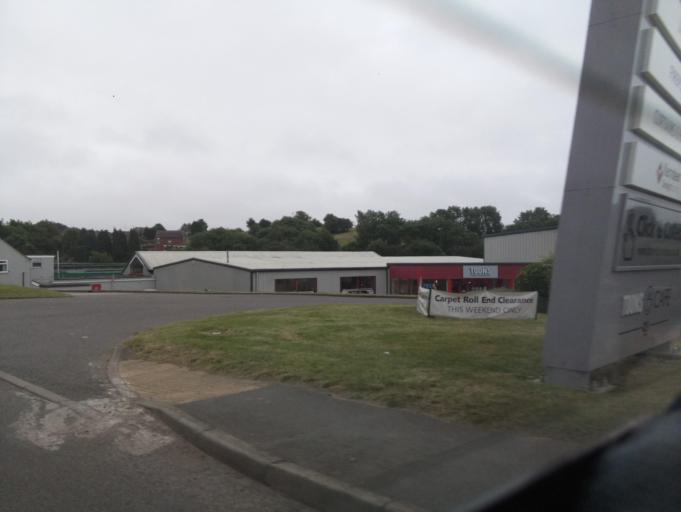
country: GB
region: England
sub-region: Derbyshire
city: Swadlincote
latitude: 52.7584
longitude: -1.5840
